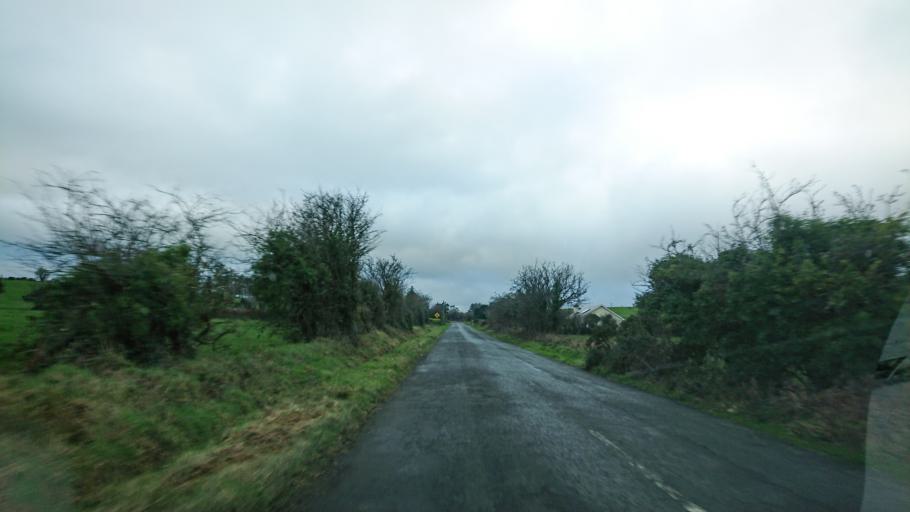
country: IE
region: Munster
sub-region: Waterford
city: Portlaw
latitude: 52.2580
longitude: -7.4036
